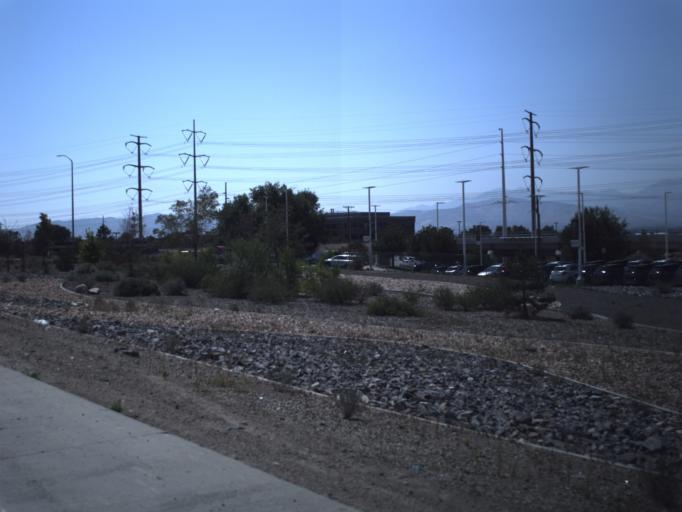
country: US
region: Utah
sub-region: Salt Lake County
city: South Jordan
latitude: 40.5601
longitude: -111.8993
